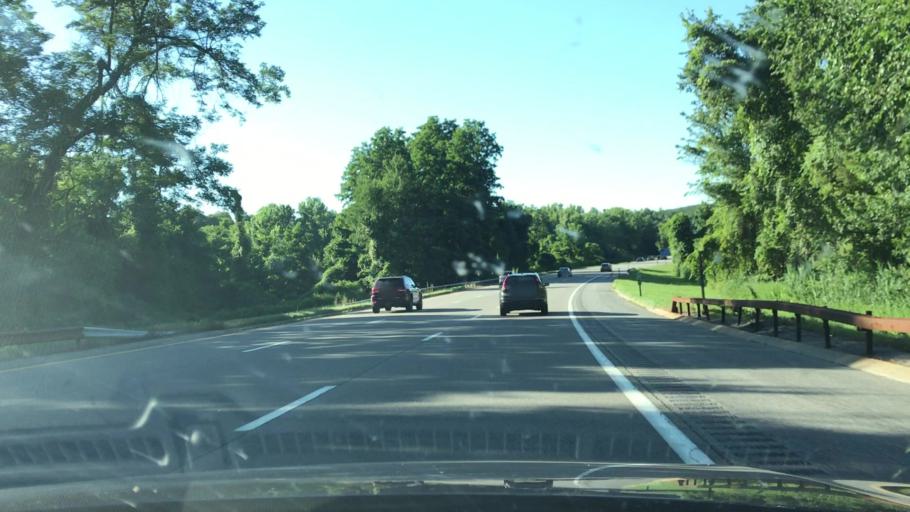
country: US
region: New York
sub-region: Westchester County
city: Briarcliff Manor
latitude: 41.2066
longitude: -73.8091
